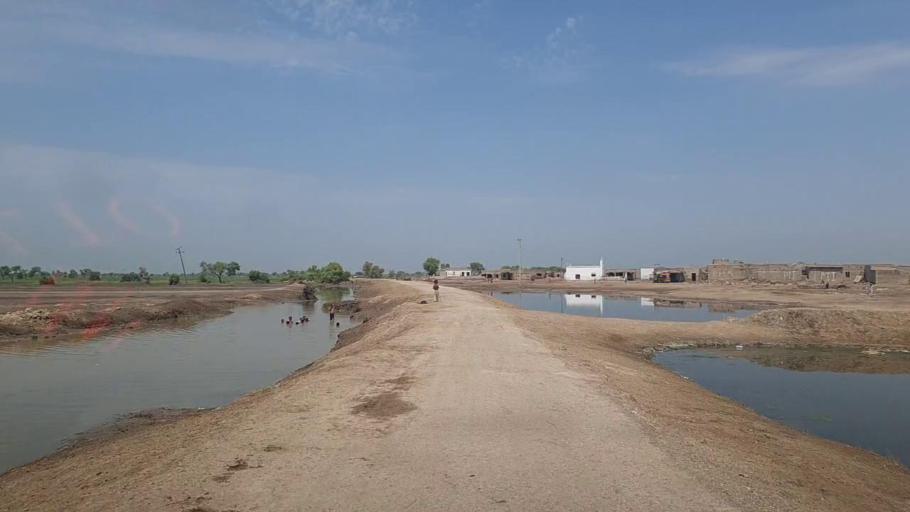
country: PK
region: Sindh
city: Thul
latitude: 28.2931
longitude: 68.6823
